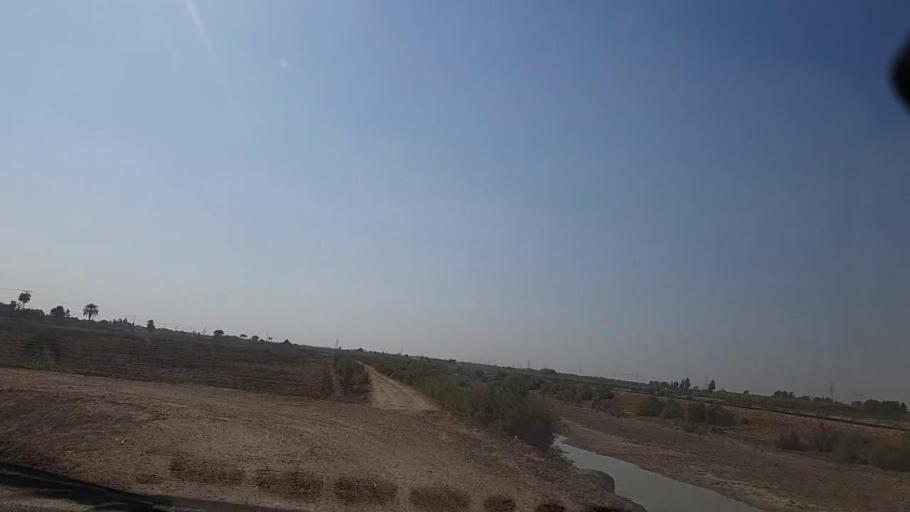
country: PK
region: Sindh
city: Mirpur Khas
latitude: 25.5086
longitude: 68.9097
